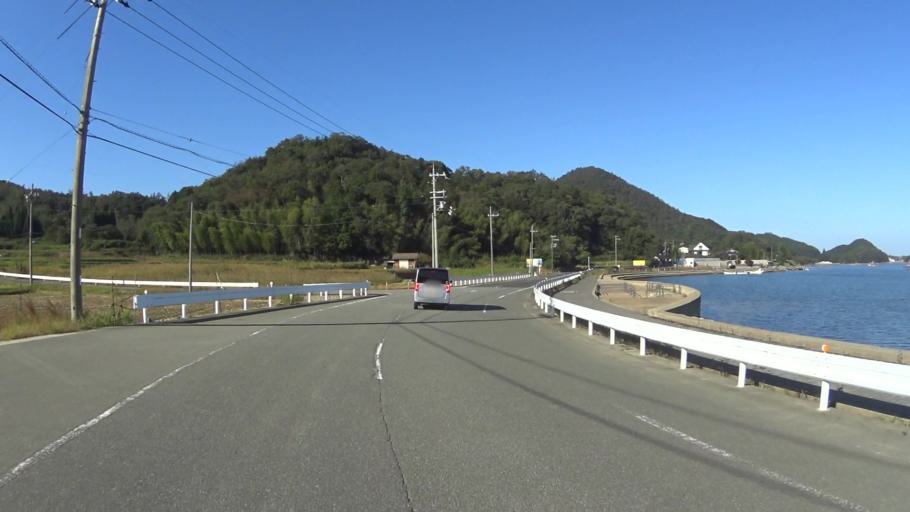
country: JP
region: Hyogo
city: Toyooka
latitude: 35.6307
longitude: 134.8877
